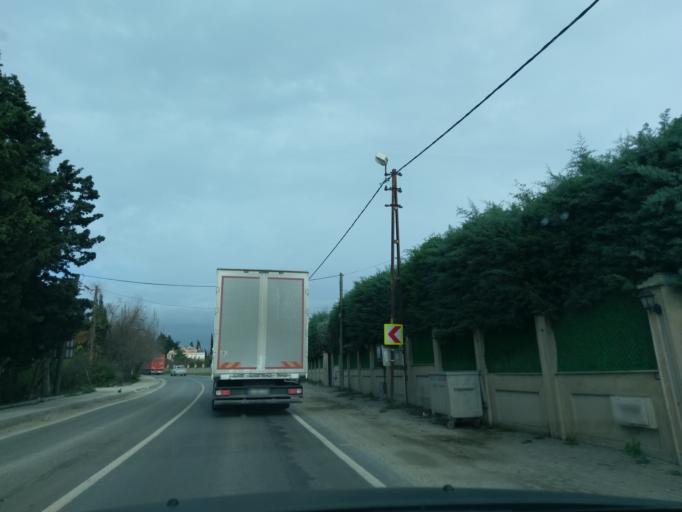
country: TR
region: Istanbul
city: Selimpasa
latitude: 41.0685
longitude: 28.3706
